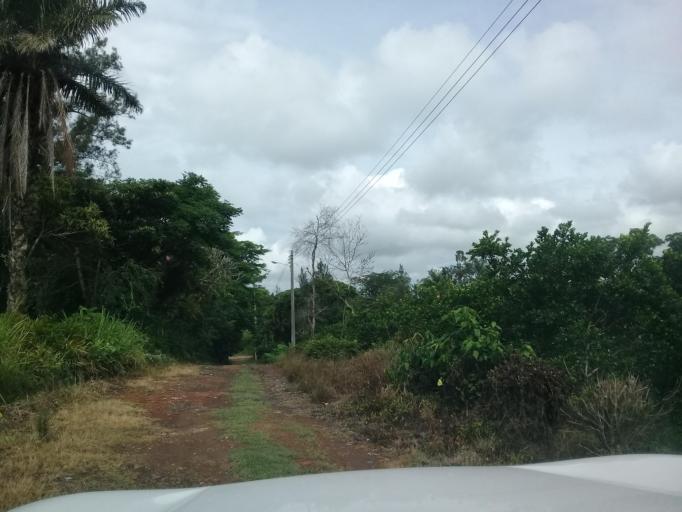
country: MX
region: Veracruz
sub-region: Emiliano Zapata
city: Jacarandas
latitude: 19.4820
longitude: -96.8521
